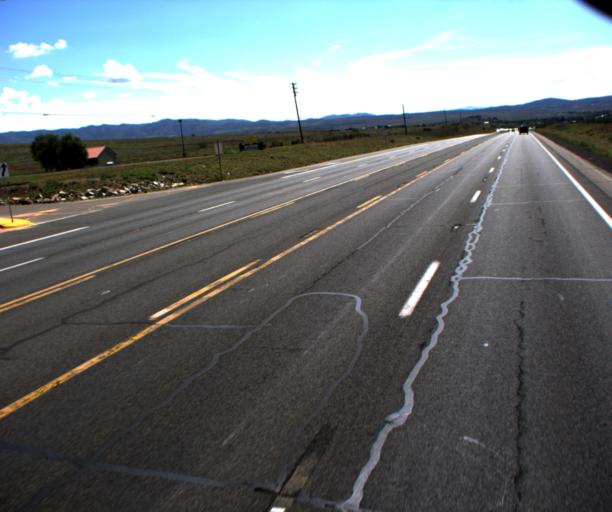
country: US
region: Arizona
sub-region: Yavapai County
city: Prescott Valley
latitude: 34.5763
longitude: -112.2884
